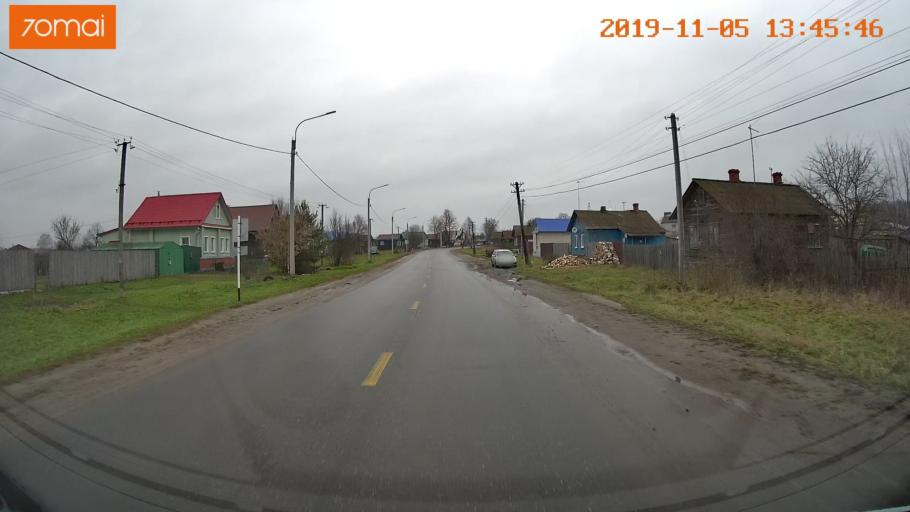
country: RU
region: Ivanovo
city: Shuya
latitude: 56.9912
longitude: 41.4116
